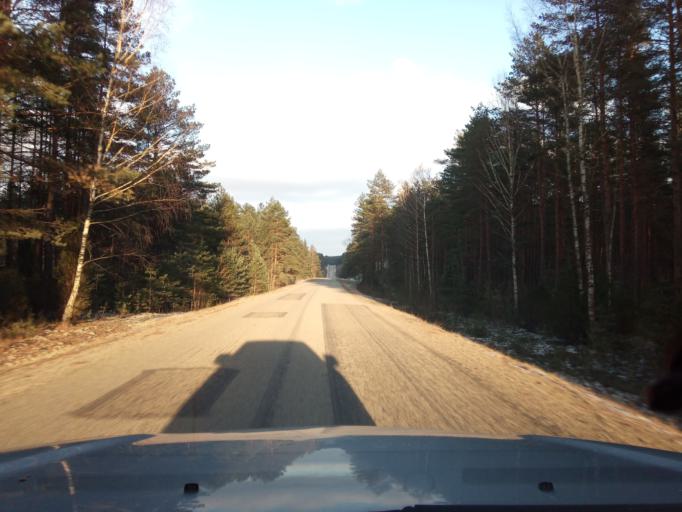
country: LT
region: Alytaus apskritis
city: Varena
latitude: 54.1250
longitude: 24.4550
